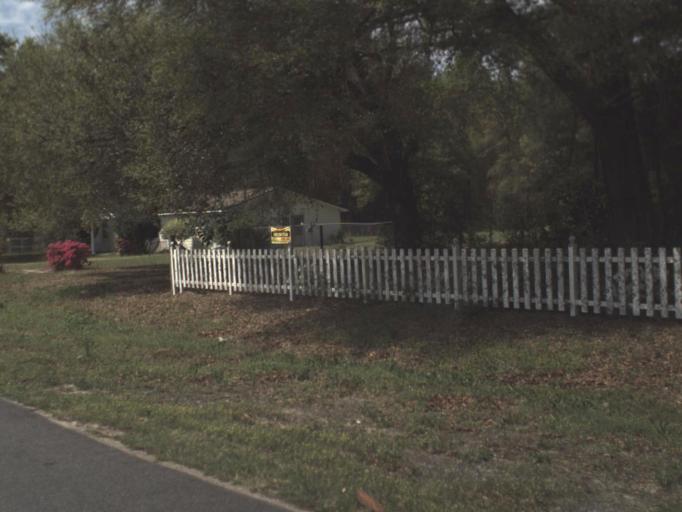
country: US
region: Florida
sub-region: Okaloosa County
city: Crestview
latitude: 30.7322
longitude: -86.6541
